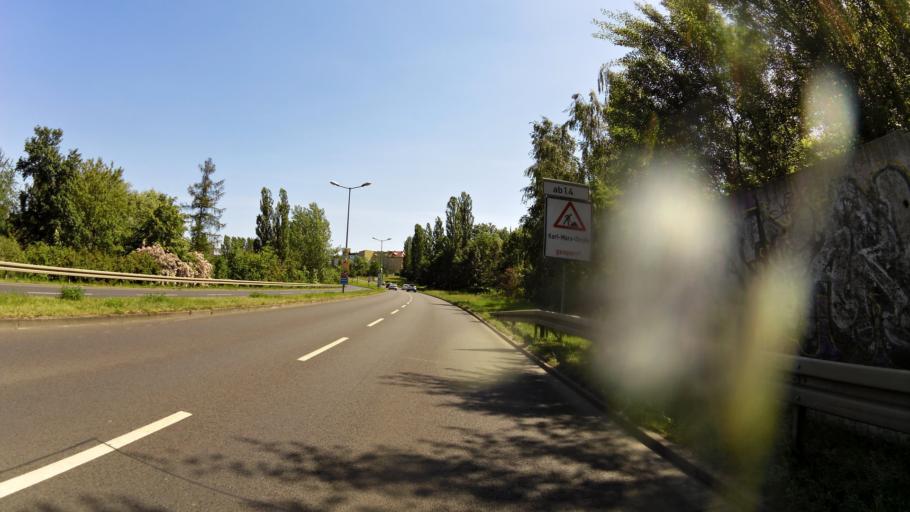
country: DE
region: Brandenburg
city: Frankfurt (Oder)
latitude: 52.3498
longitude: 14.5325
